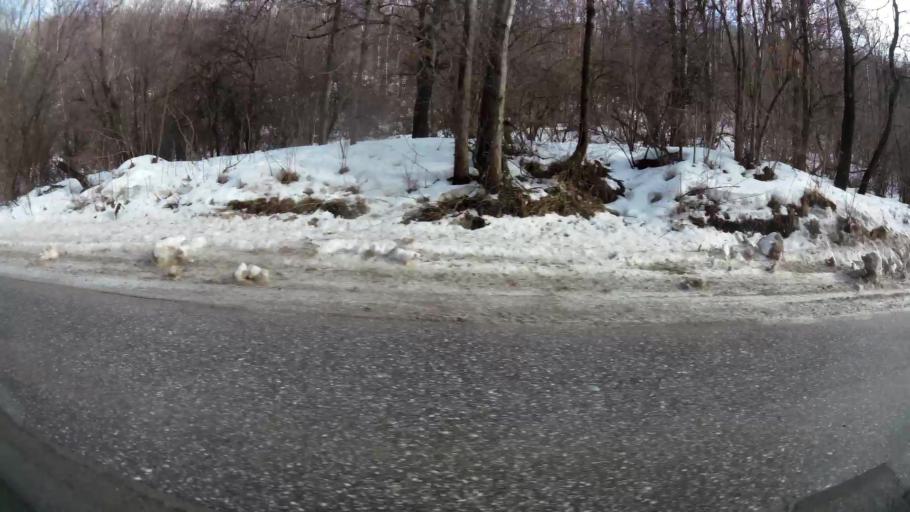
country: BG
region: Sofia-Capital
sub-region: Stolichna Obshtina
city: Sofia
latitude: 42.6314
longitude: 23.2299
